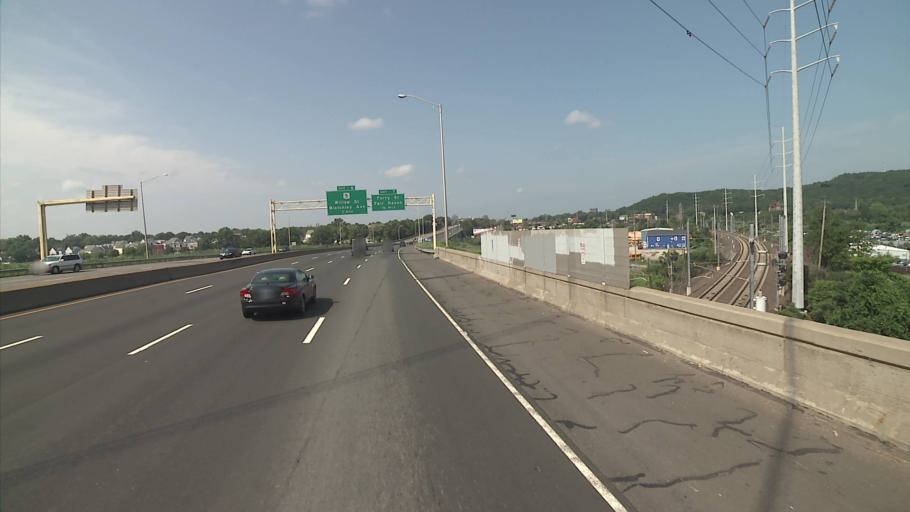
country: US
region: Connecticut
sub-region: New Haven County
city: New Haven
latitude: 41.3226
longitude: -72.8854
